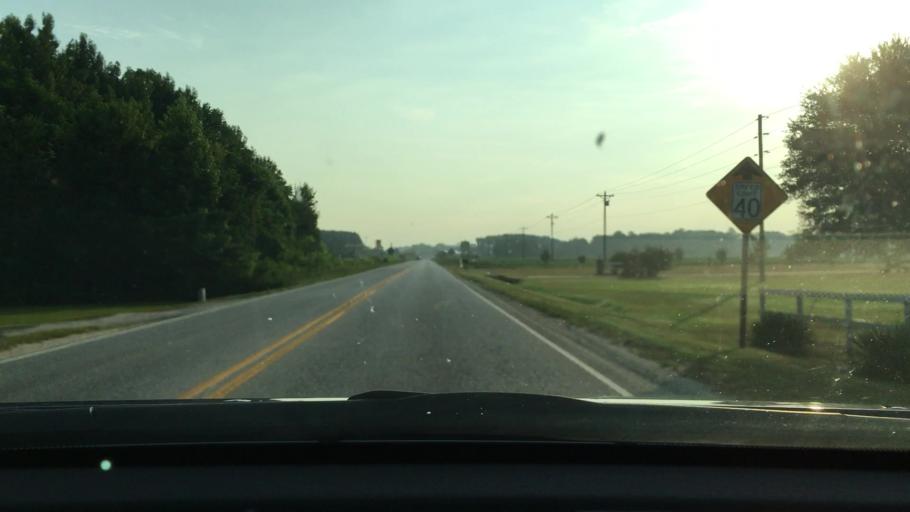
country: US
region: South Carolina
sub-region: Florence County
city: Timmonsville
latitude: 34.2011
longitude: -80.0332
